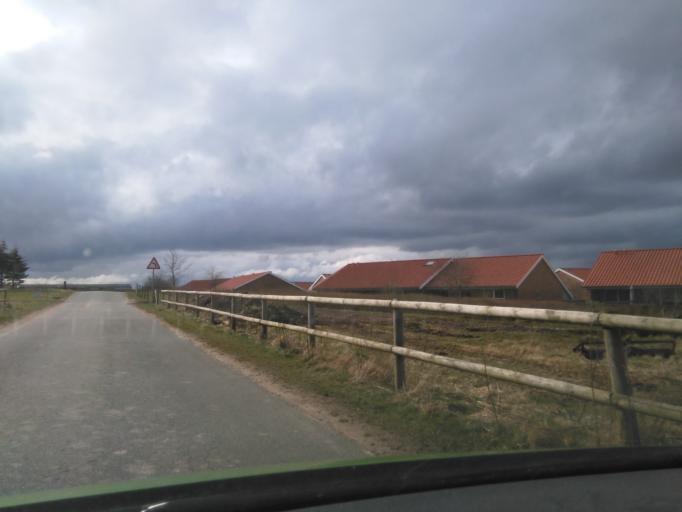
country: DK
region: Central Jutland
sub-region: Arhus Kommune
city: Marslet
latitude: 56.1031
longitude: 10.1787
